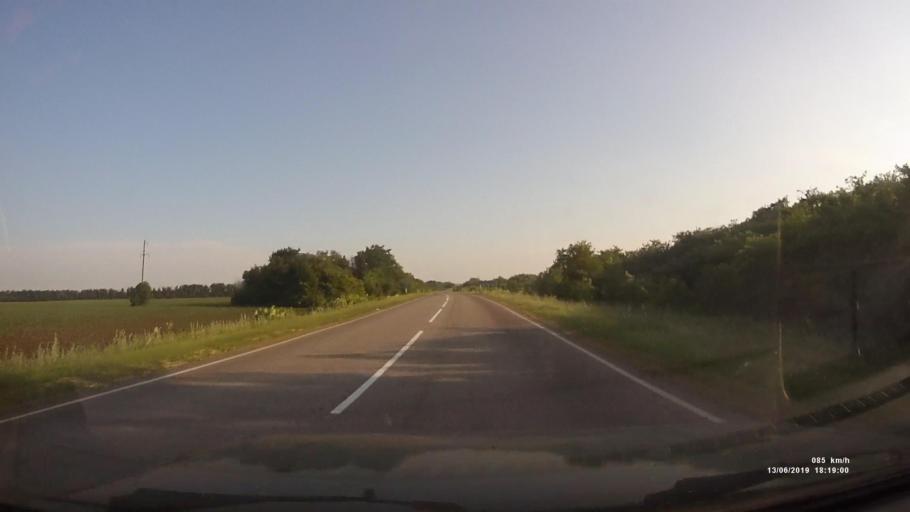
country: RU
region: Rostov
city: Kazanskaya
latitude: 49.9015
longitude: 41.3092
